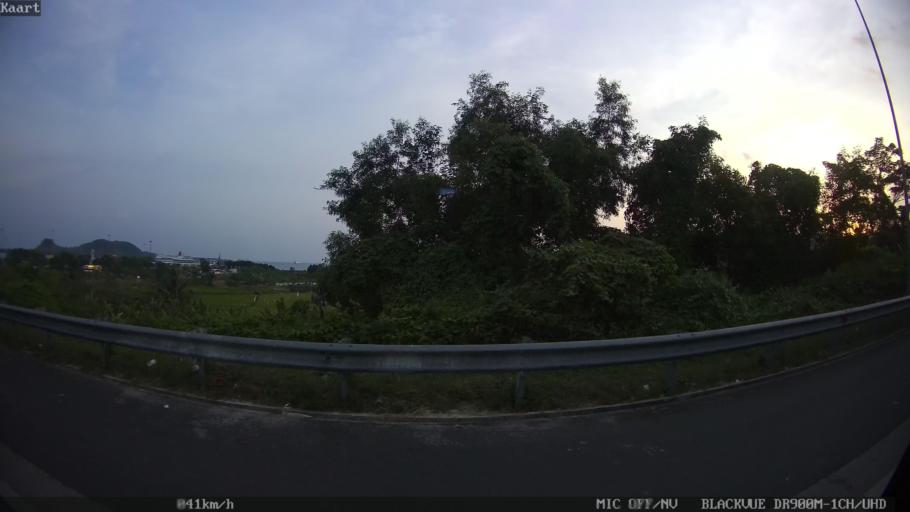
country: ID
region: Lampung
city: Penengahan
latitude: -5.8688
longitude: 105.7506
